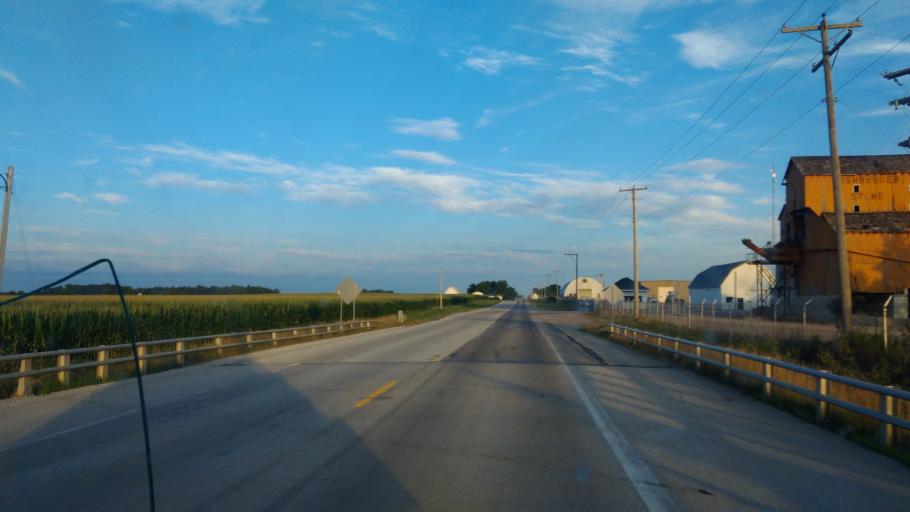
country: US
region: Indiana
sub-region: Adams County
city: Berne
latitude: 40.6557
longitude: -85.0510
